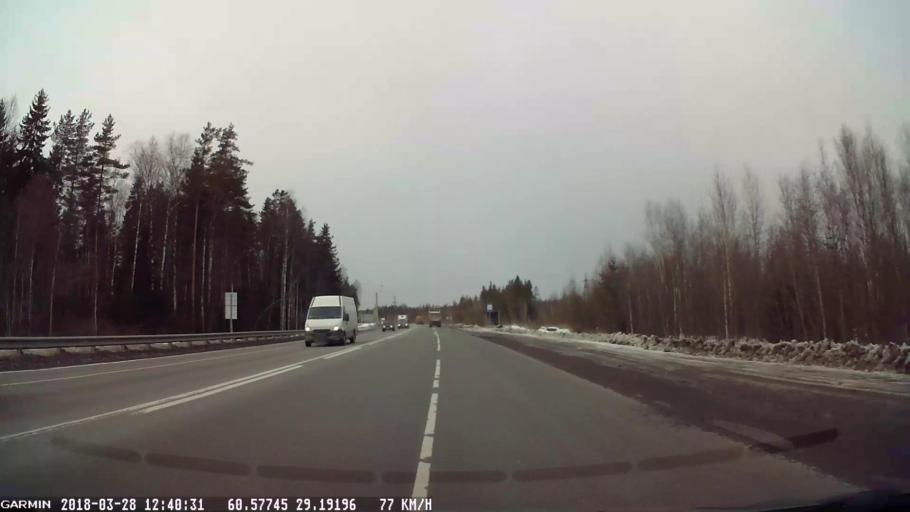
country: RU
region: Leningrad
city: Veshchevo
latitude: 60.5775
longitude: 29.1919
